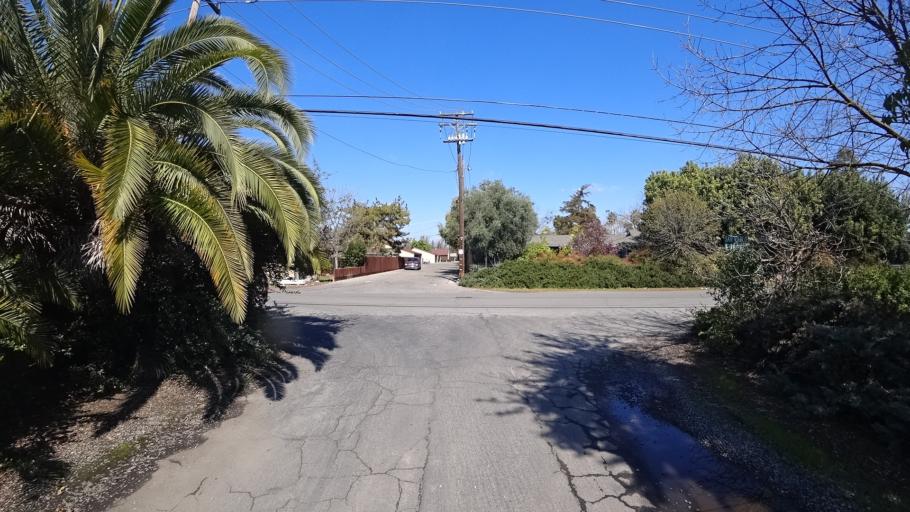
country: US
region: California
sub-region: Fresno County
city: Fresno
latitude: 36.7994
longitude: -119.7939
